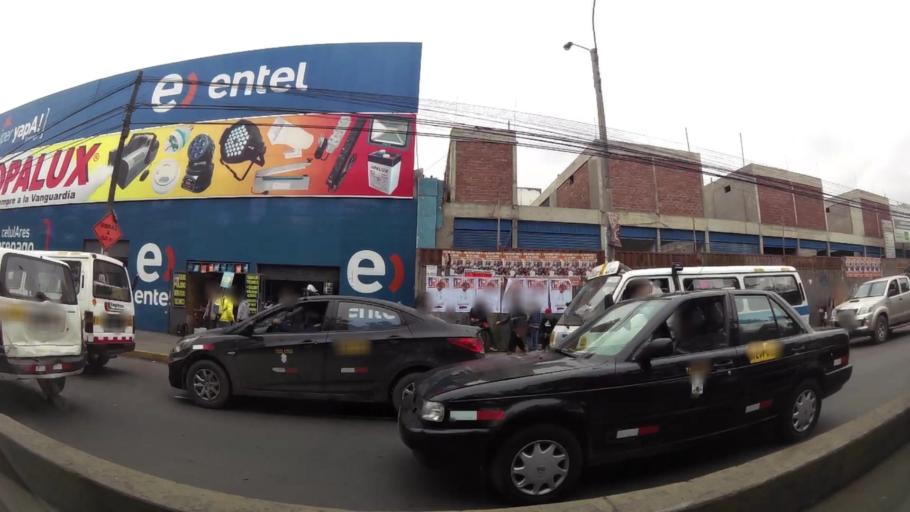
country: PE
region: Lima
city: Lima
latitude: -12.0435
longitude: -77.0463
